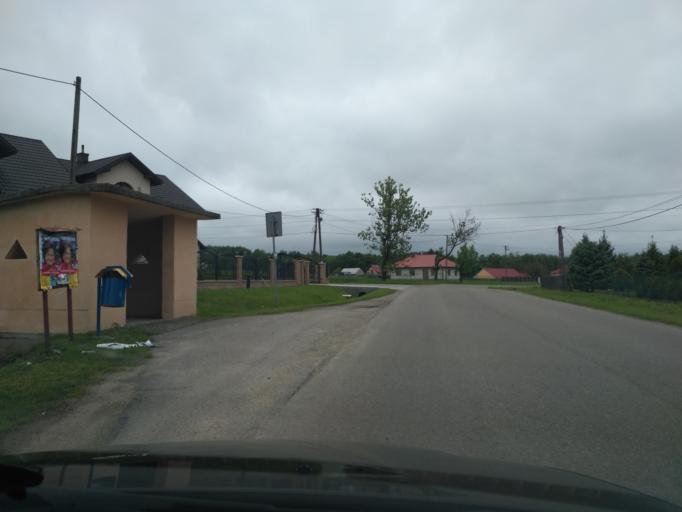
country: PL
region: Subcarpathian Voivodeship
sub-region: Powiat jasielski
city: Brzyska
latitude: 49.8403
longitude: 21.3879
